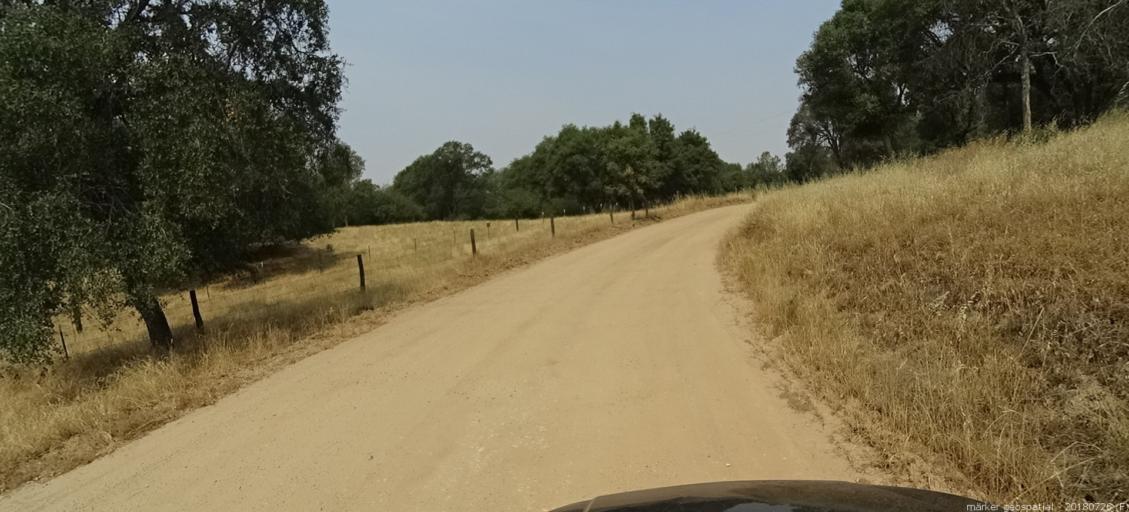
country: US
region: California
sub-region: Madera County
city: Coarsegold
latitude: 37.2424
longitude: -119.6790
